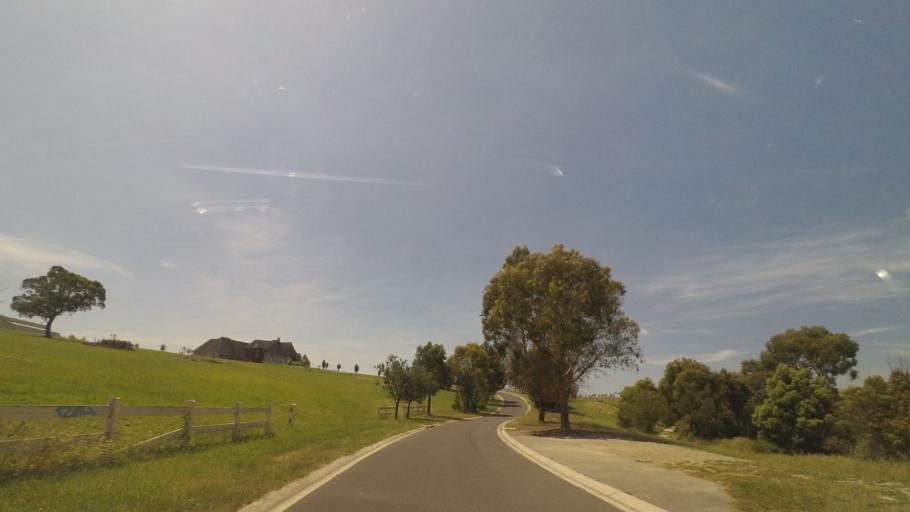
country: AU
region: Victoria
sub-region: Yarra Ranges
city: Chirnside Park
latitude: -37.7484
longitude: 145.3092
